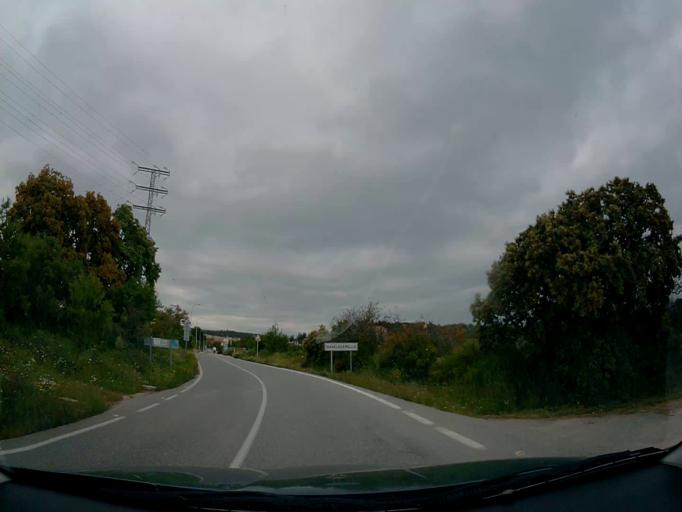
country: ES
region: Madrid
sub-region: Provincia de Madrid
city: Navalagamella
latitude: 40.4652
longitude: -4.1183
